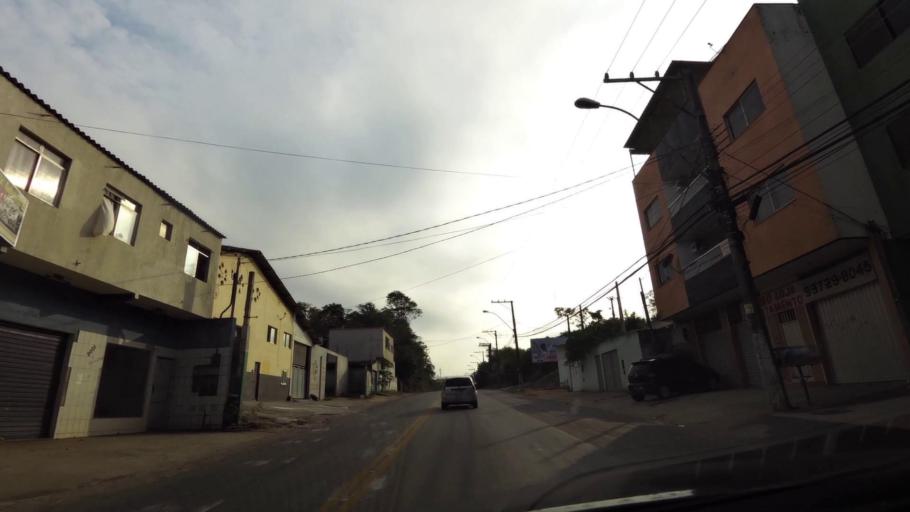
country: BR
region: Espirito Santo
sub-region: Guarapari
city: Guarapari
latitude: -20.6382
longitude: -40.4818
